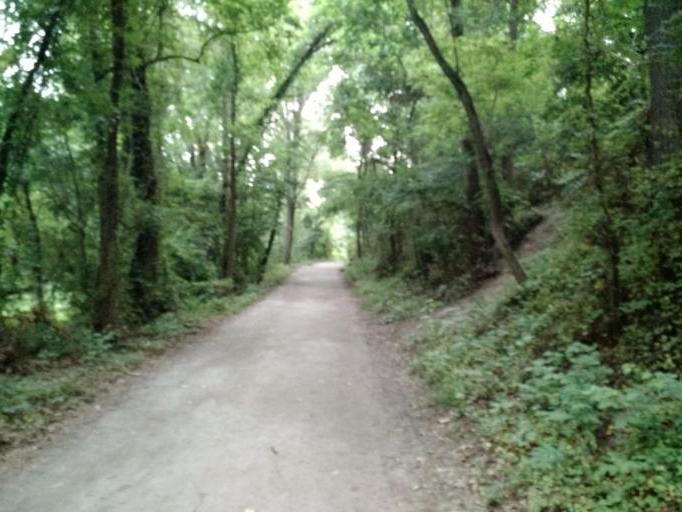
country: US
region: Virginia
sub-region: City of Richmond
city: Richmond
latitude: 37.5276
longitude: -77.4553
